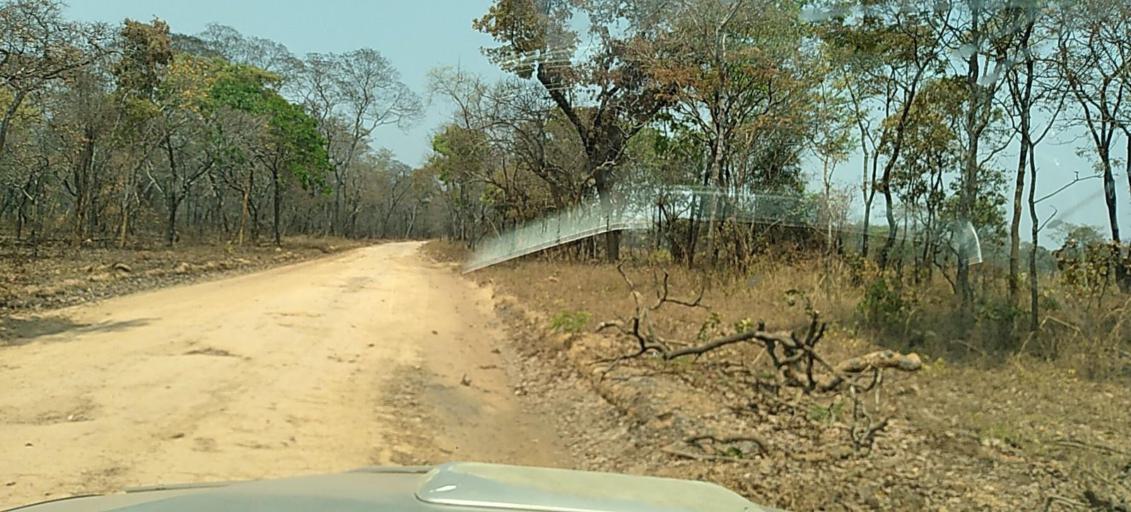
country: ZM
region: North-Western
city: Kasempa
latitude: -13.6140
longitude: 26.1984
